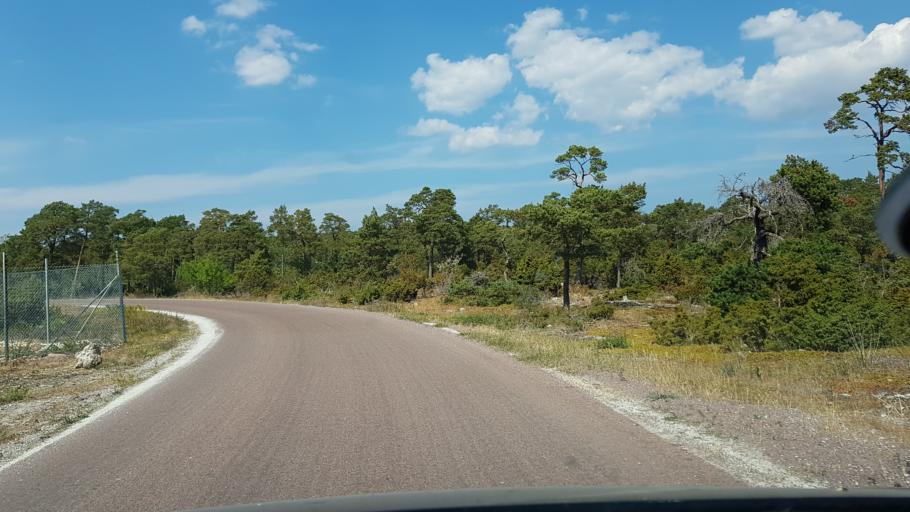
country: SE
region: Gotland
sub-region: Gotland
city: Visby
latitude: 57.6833
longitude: 18.3643
